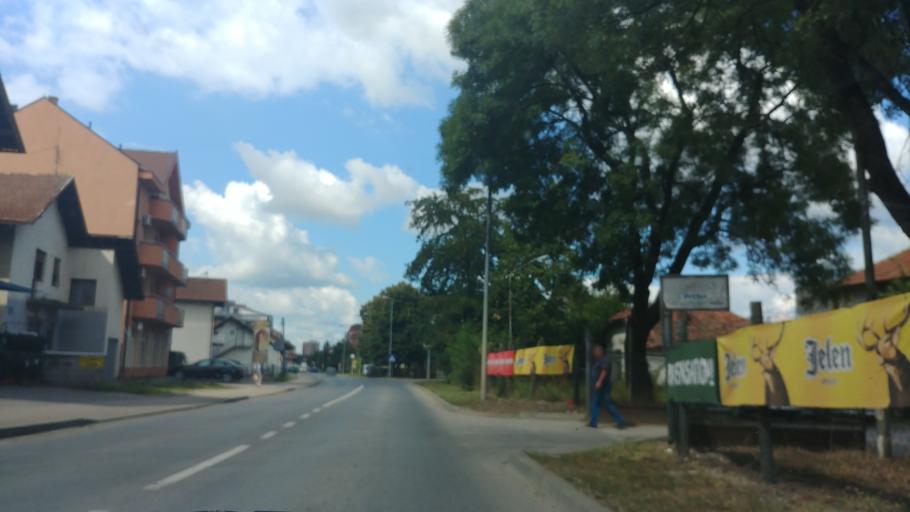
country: BA
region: Brcko
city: Brcko
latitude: 44.8669
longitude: 18.8198
